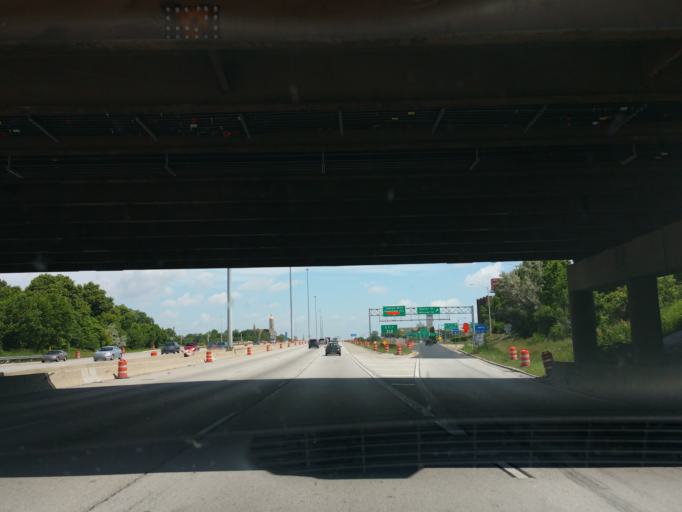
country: US
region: Wisconsin
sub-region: Milwaukee County
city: Milwaukee
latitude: 43.0027
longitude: -87.9161
